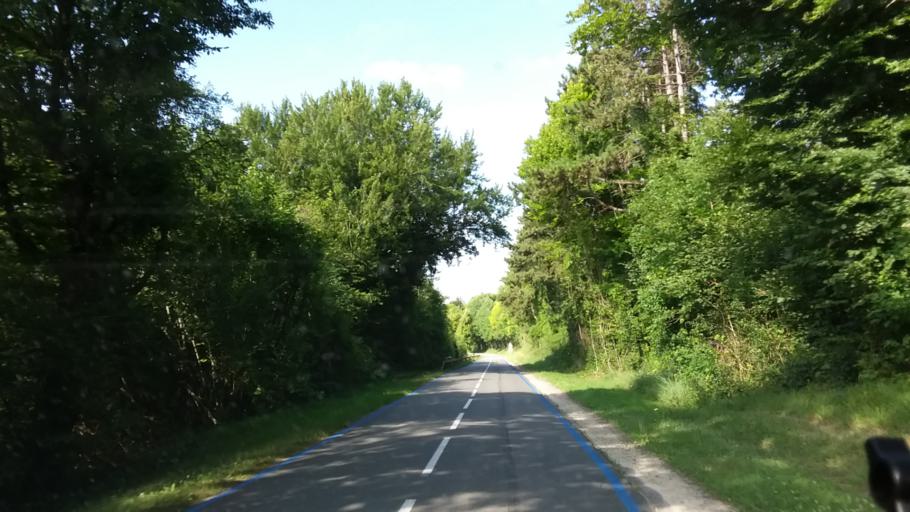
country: FR
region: Picardie
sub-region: Departement de l'Aisne
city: Saint-Erme-Outre-et-Ramecourt
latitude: 49.4444
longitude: 3.7735
